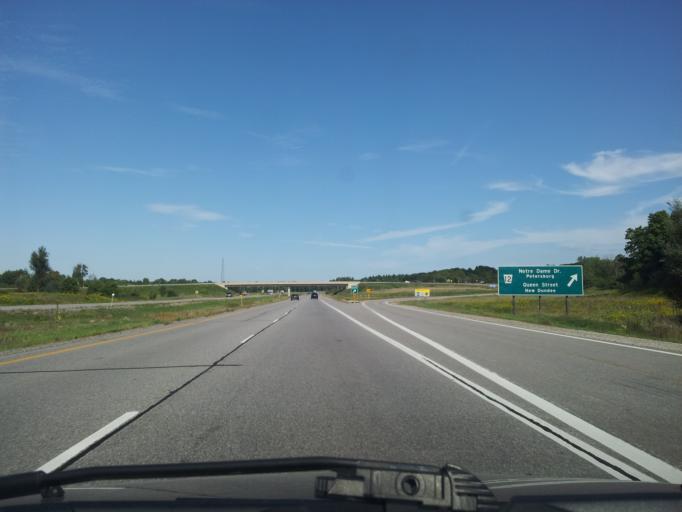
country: CA
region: Ontario
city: Kitchener
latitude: 43.4044
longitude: -80.6019
